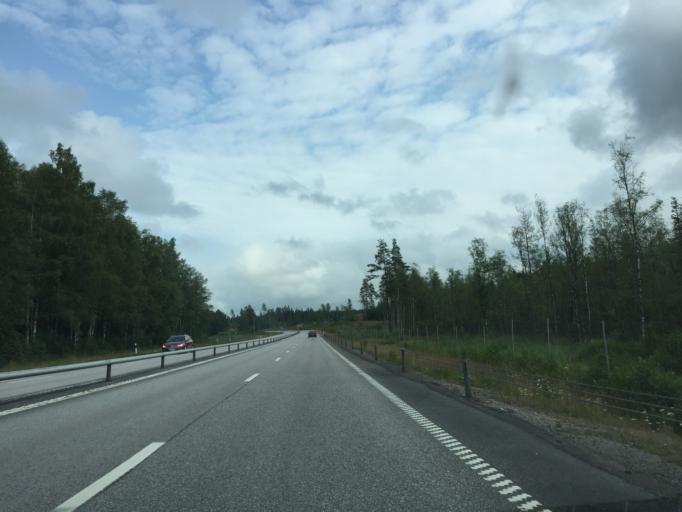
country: SE
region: OErebro
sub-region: Karlskoga Kommun
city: Karlskoga
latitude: 59.2797
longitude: 14.7012
